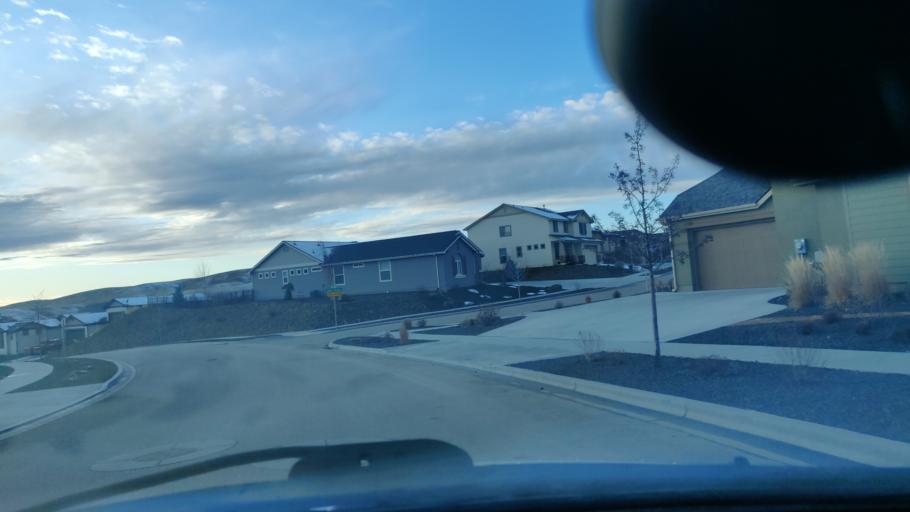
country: US
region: Idaho
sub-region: Ada County
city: Eagle
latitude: 43.7738
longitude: -116.2524
